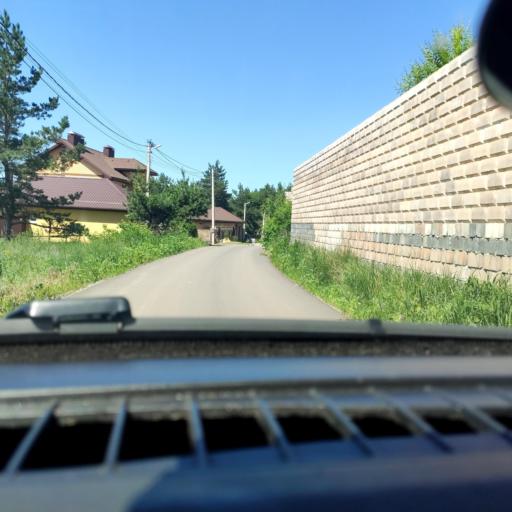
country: RU
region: Voronezj
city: Podgornoye
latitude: 51.7933
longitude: 39.1353
